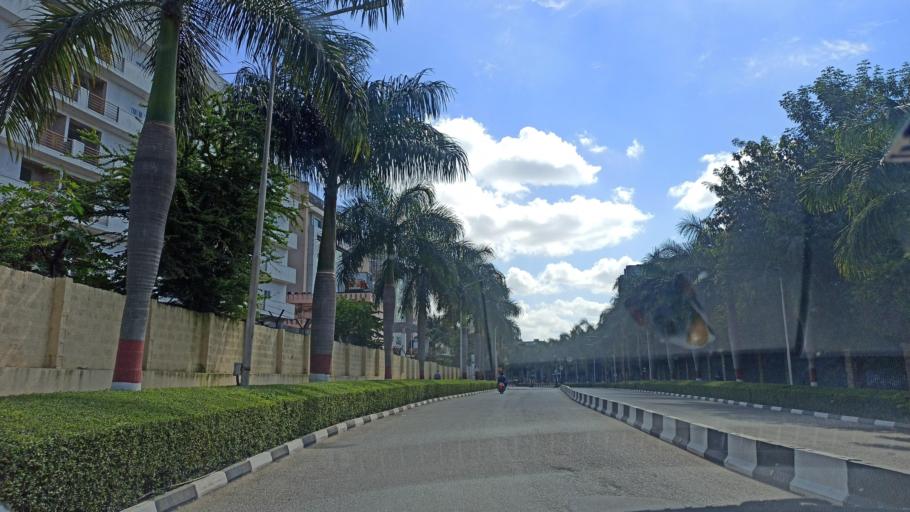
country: IN
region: Karnataka
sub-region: Bangalore Urban
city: Bangalore
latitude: 12.9270
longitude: 77.6858
